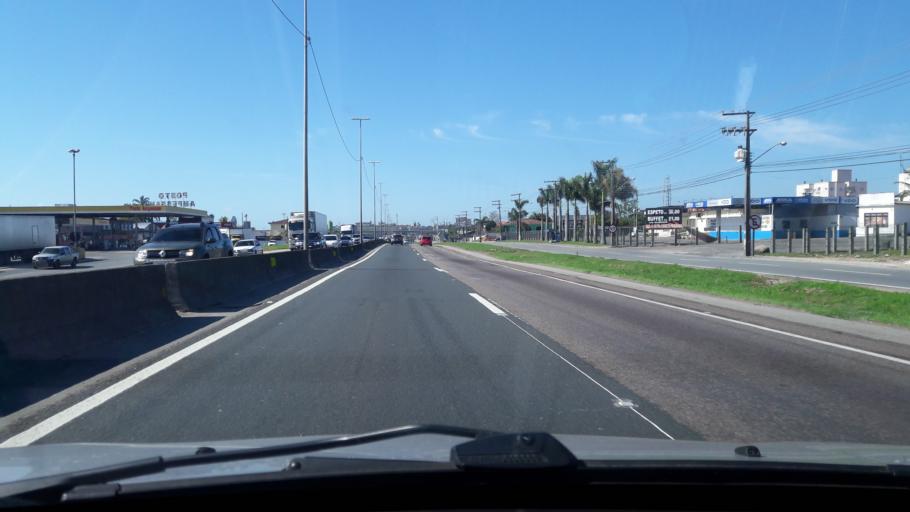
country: BR
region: Santa Catarina
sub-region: Biguacu
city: Biguacu
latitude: -27.5252
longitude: -48.6359
